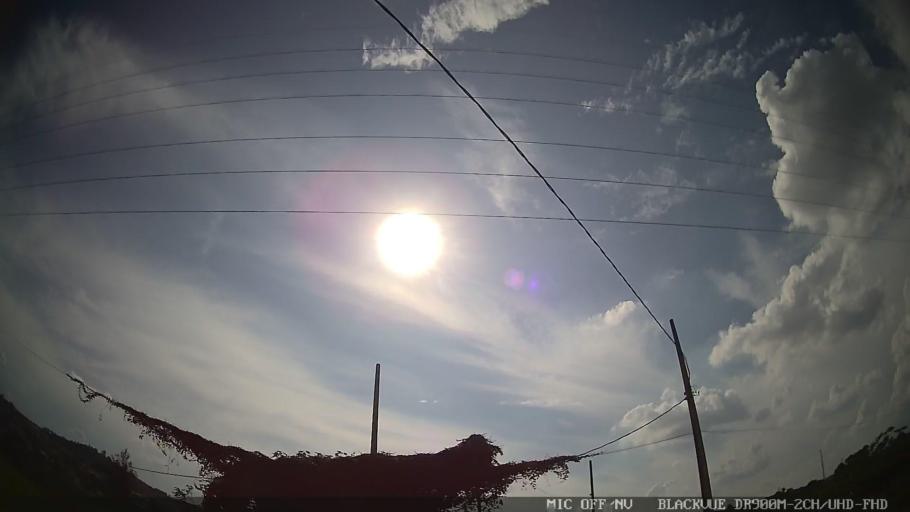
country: BR
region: Sao Paulo
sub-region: Braganca Paulista
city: Braganca Paulista
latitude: -22.9407
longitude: -46.5565
